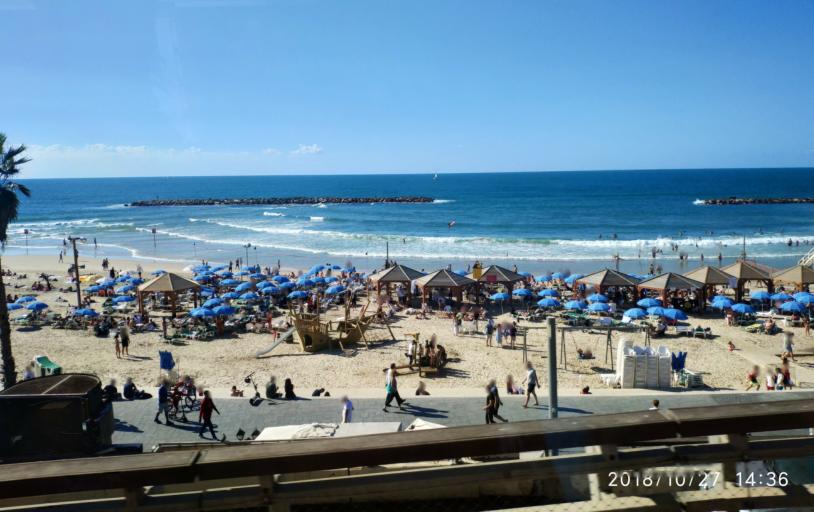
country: IL
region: Tel Aviv
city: Tel Aviv
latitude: 32.0820
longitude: 34.7679
